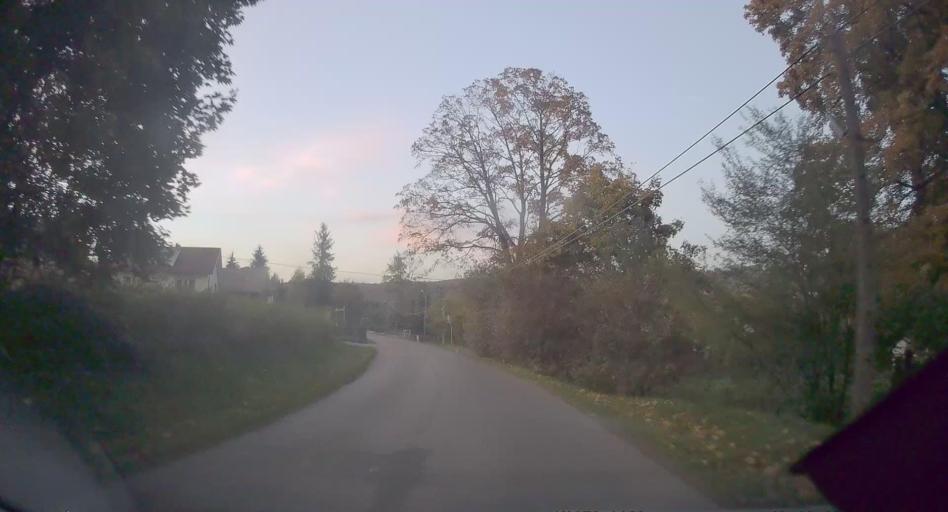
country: PL
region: Lesser Poland Voivodeship
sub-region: Powiat krakowski
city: Bolechowice
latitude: 50.1391
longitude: 19.8158
